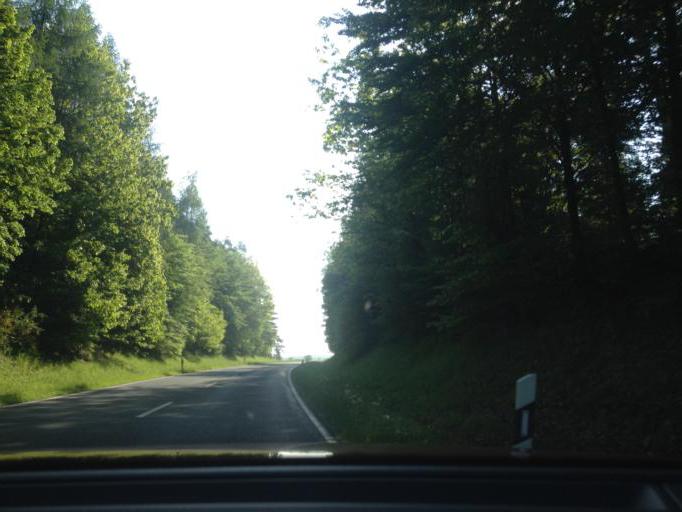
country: DE
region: Bavaria
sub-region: Upper Franconia
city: Creussen
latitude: 49.7742
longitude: 11.6398
